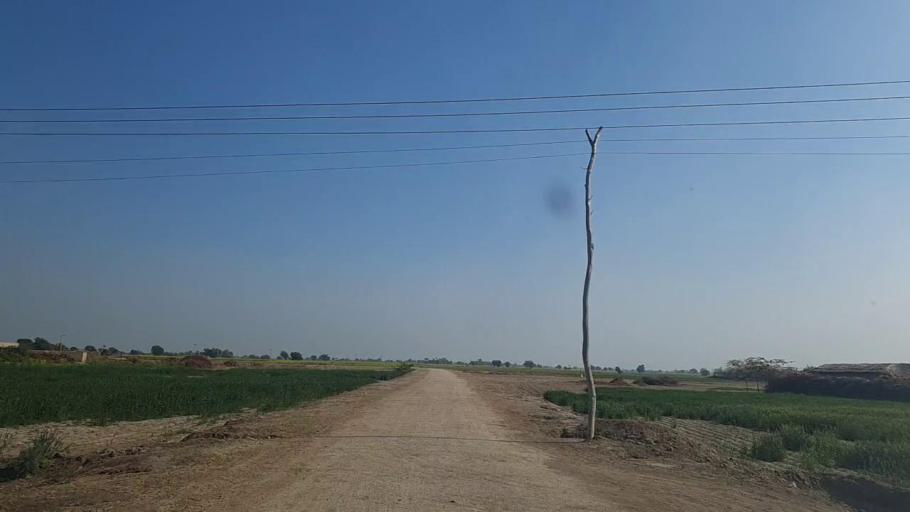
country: PK
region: Sindh
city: Shahpur Chakar
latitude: 26.1964
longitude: 68.5937
